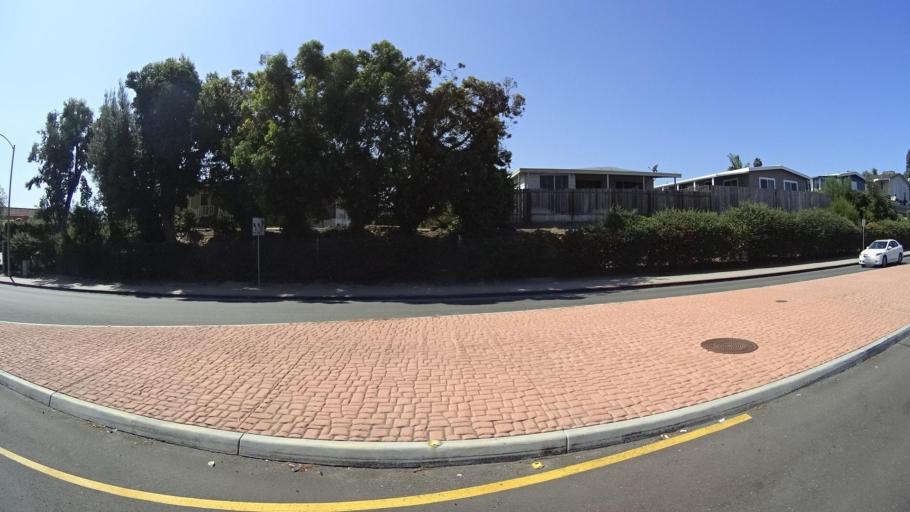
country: US
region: California
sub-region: San Diego County
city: Lake San Marcos
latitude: 33.1495
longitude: -117.1998
